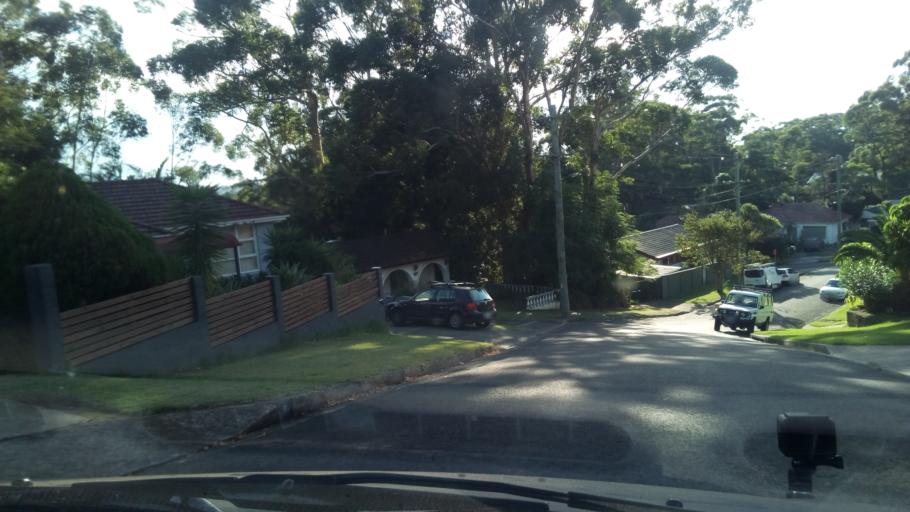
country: AU
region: New South Wales
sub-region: Wollongong
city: Mount Ousley
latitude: -34.3963
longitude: 150.8707
